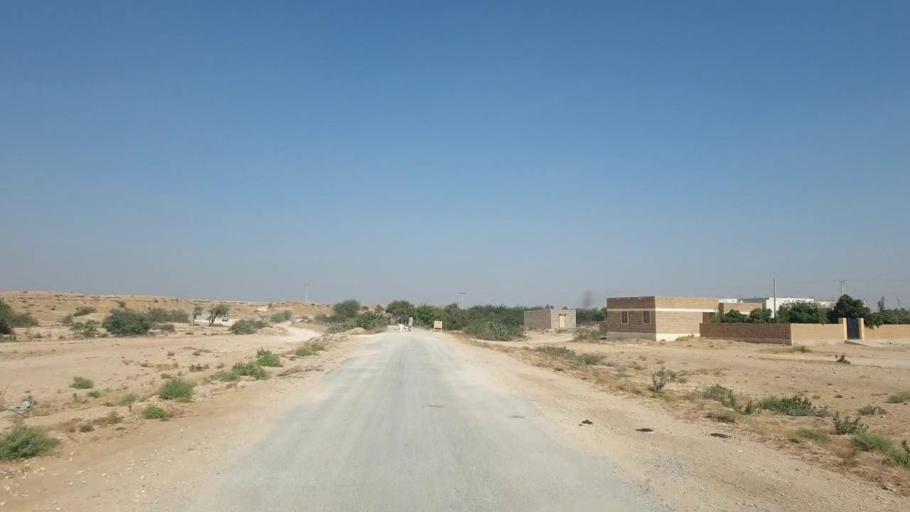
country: PK
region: Sindh
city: Thatta
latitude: 25.2161
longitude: 67.7957
